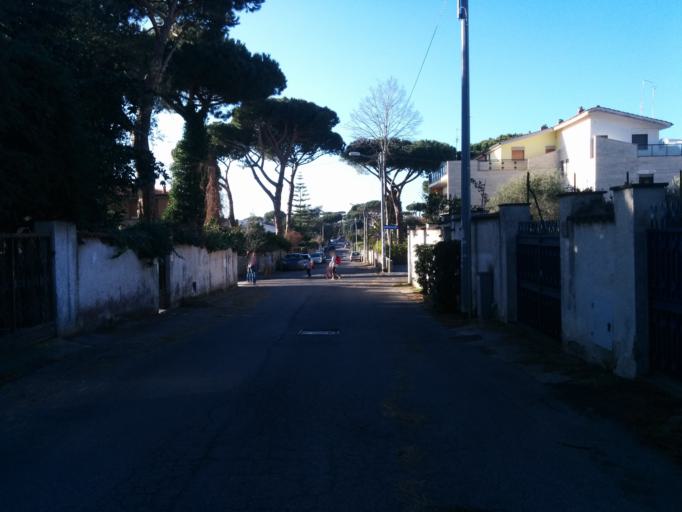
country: IT
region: Latium
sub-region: Citta metropolitana di Roma Capitale
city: Lavinio
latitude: 41.5001
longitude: 12.5962
